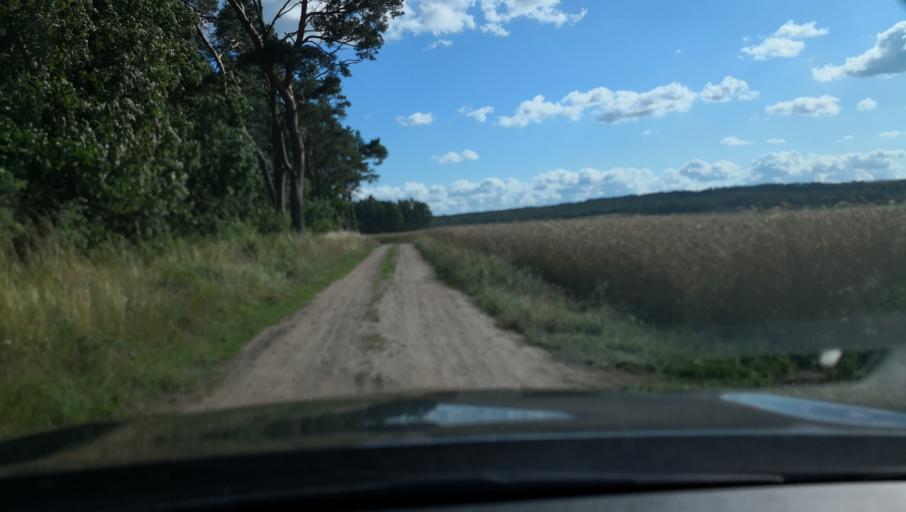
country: SE
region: Skane
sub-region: Kristianstads Kommun
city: Degeberga
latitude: 55.8017
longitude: 14.1961
